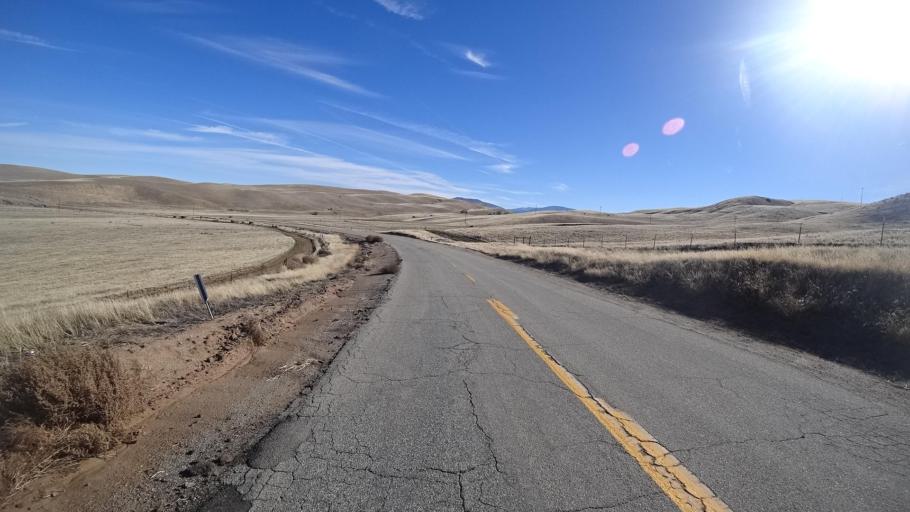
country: US
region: California
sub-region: Kern County
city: Maricopa
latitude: 34.9338
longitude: -119.4064
